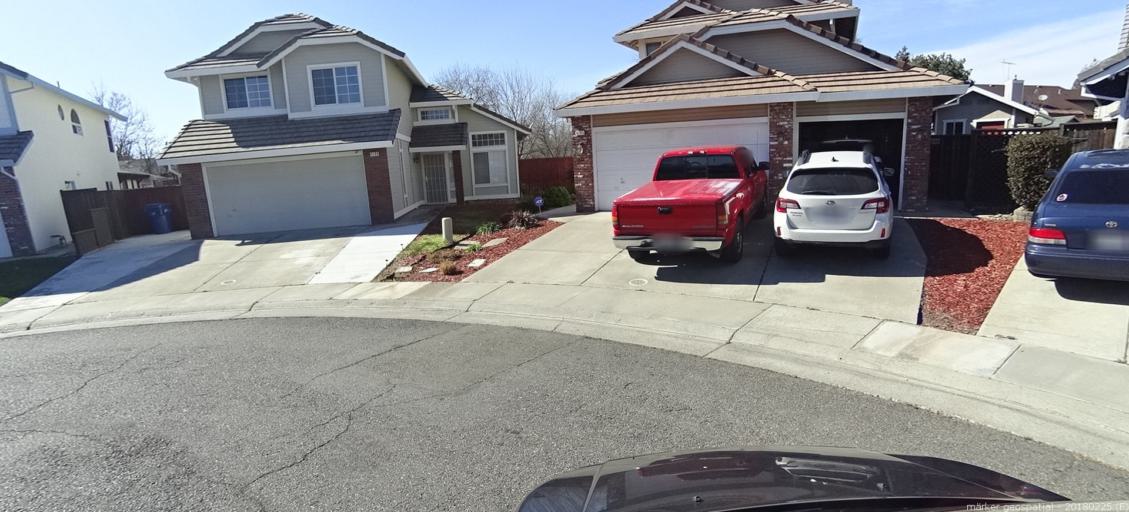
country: US
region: California
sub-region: Sacramento County
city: North Highlands
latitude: 38.7244
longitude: -121.3667
